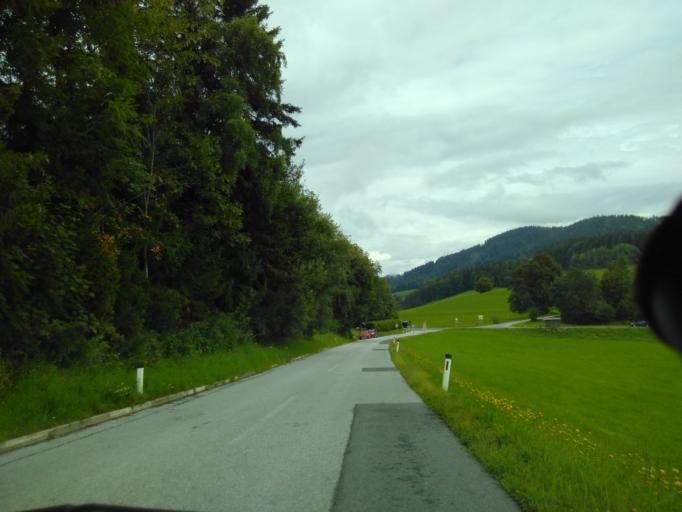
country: AT
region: Styria
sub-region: Politischer Bezirk Graz-Umgebung
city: Semriach
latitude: 47.2673
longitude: 15.4157
